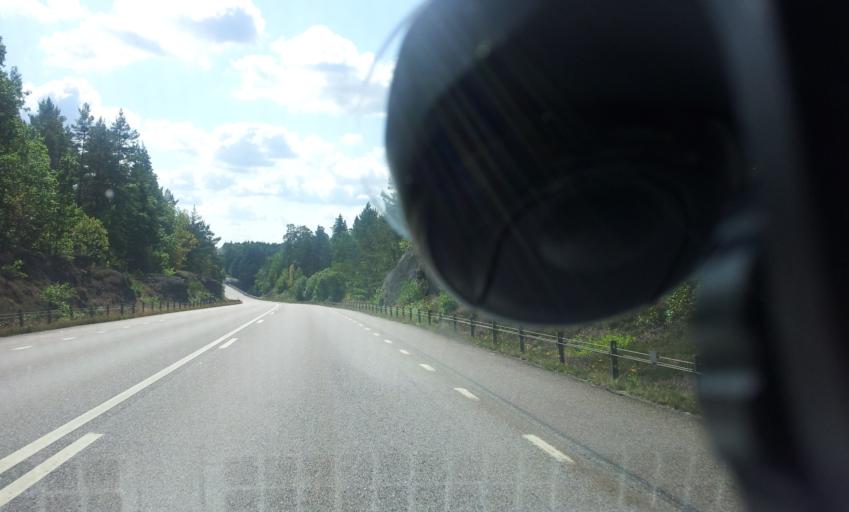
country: SE
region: Kalmar
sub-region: Vasterviks Kommun
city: Ankarsrum
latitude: 57.5544
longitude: 16.4749
